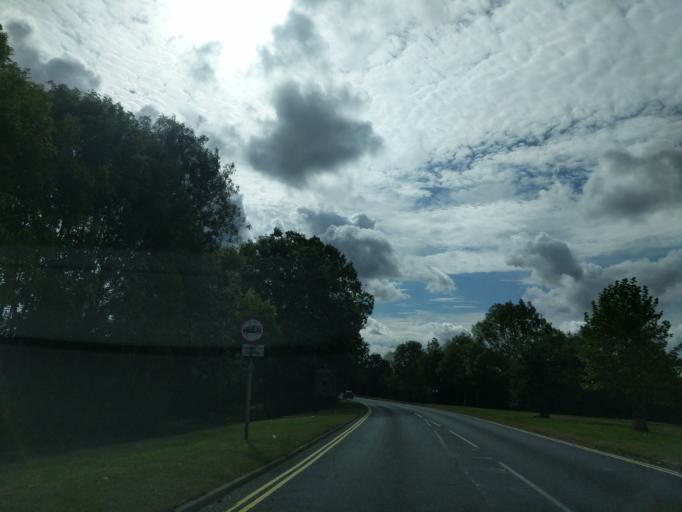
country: GB
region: England
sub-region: Oxfordshire
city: Oxford
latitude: 51.7741
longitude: -1.2294
